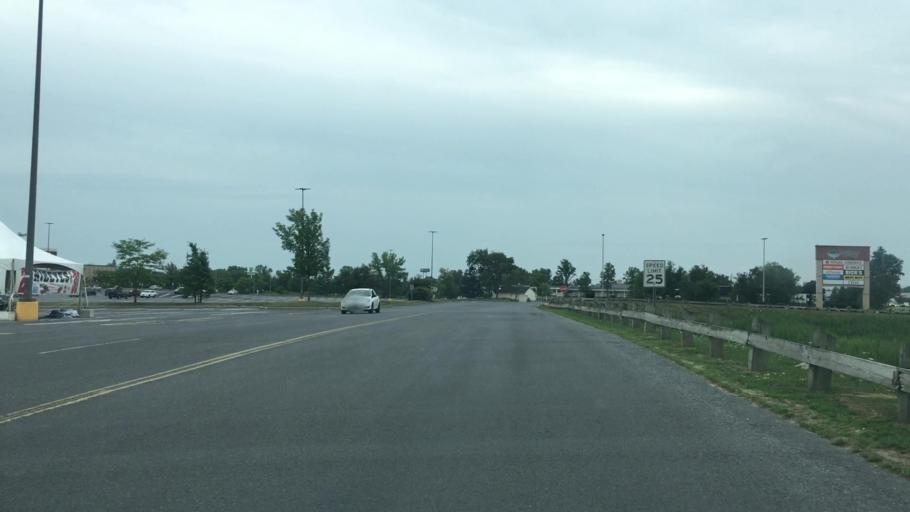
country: US
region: New York
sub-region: Clinton County
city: Plattsburgh West
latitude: 44.7017
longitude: -73.4934
